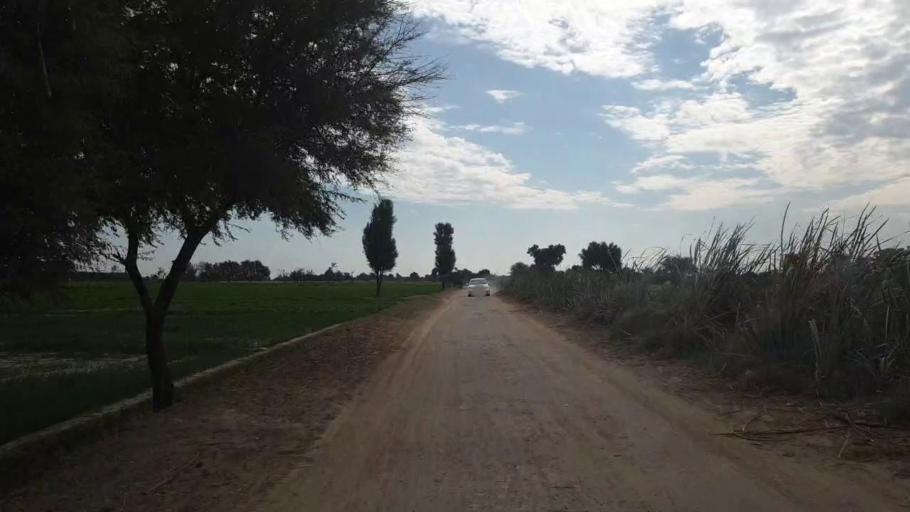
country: PK
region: Sindh
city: Jhol
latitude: 25.9919
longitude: 68.8982
